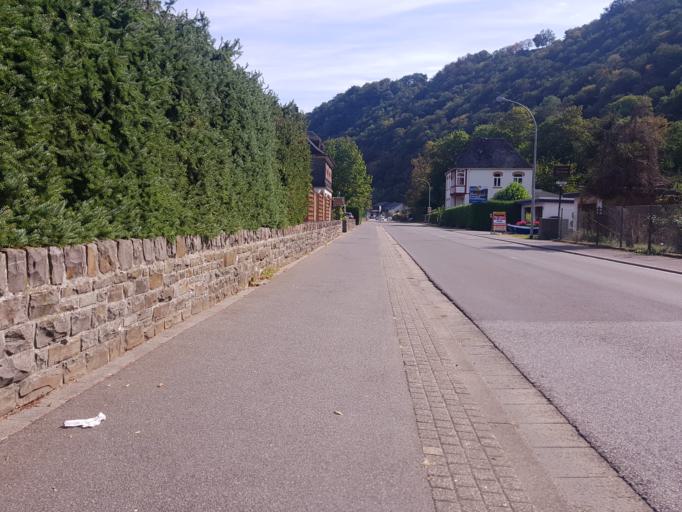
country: DE
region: Rheinland-Pfalz
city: Urbar
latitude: 50.1393
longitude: 7.7235
